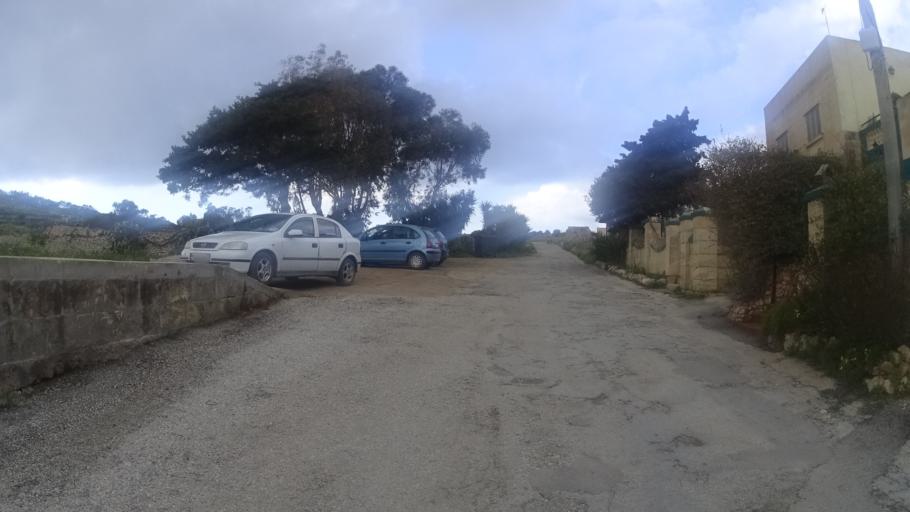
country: MT
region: L-Imgarr
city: Imgarr
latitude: 35.8960
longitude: 14.3676
